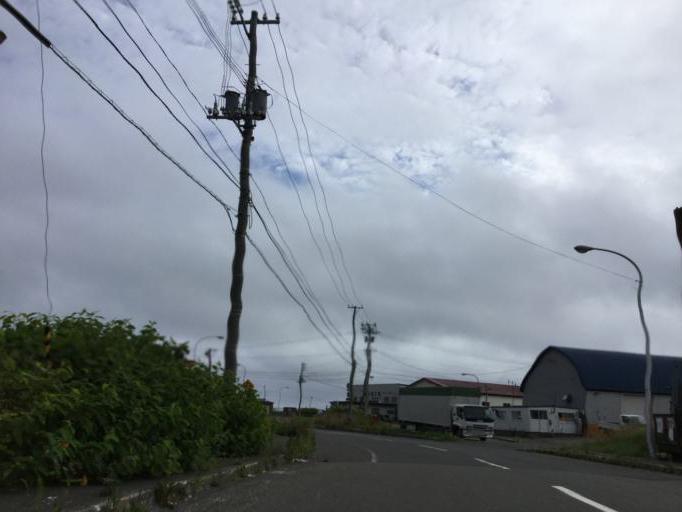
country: JP
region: Hokkaido
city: Wakkanai
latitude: 45.4007
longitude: 141.6900
